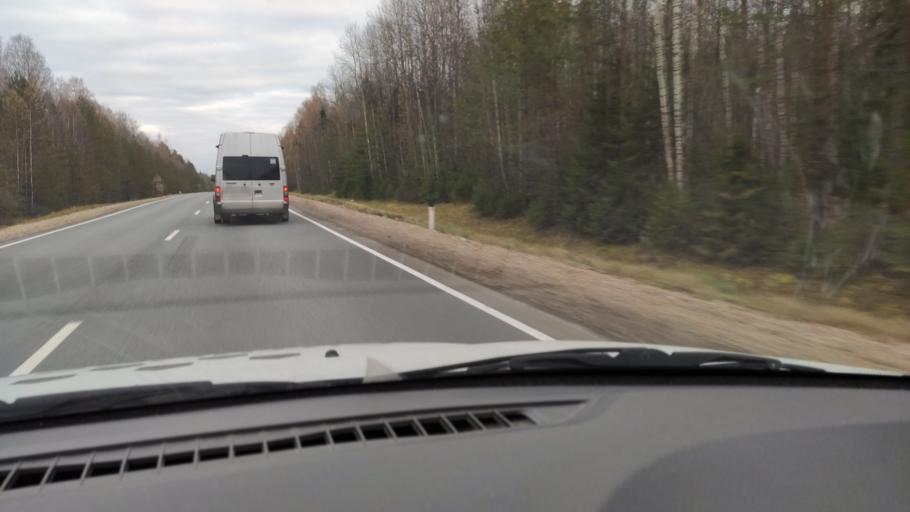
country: RU
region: Kirov
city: Chernaya Kholunitsa
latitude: 58.8588
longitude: 51.6497
